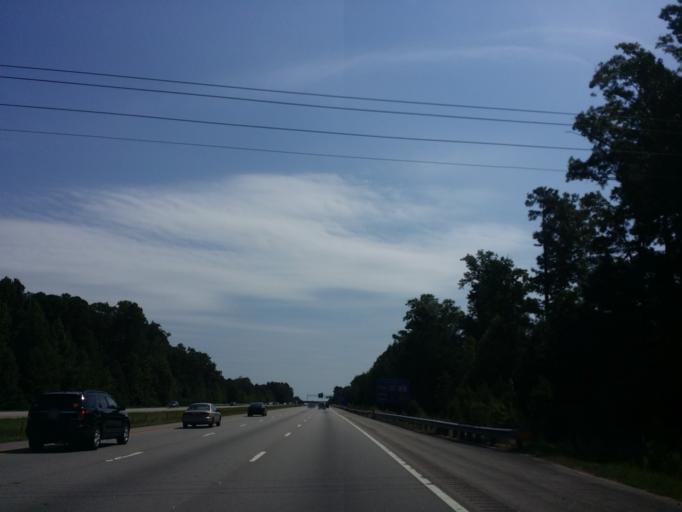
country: US
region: North Carolina
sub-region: Wake County
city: Morrisville
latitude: 35.9091
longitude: -78.7403
